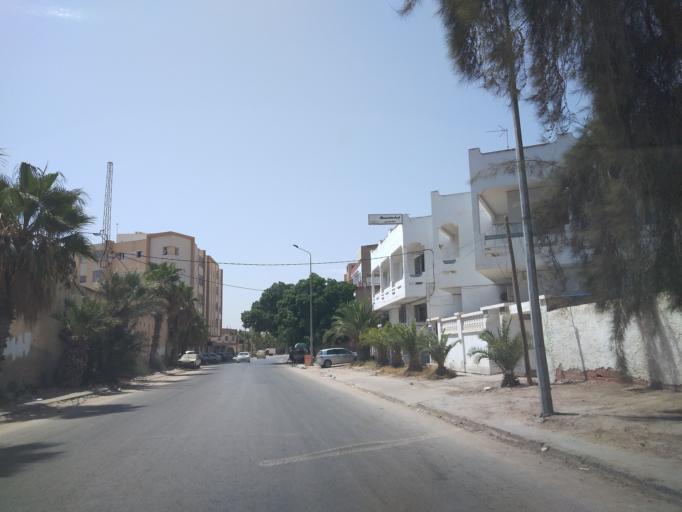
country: TN
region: Safaqis
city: Sfax
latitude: 34.7402
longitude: 10.7450
